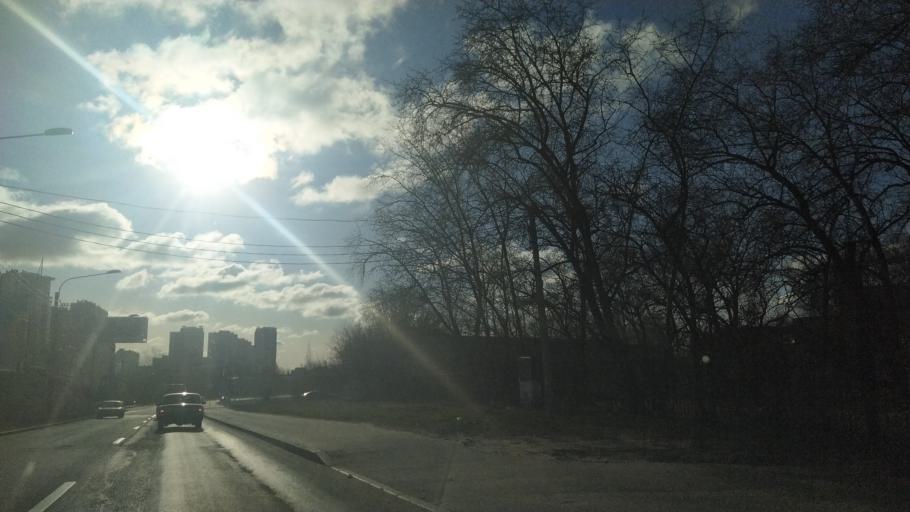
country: RU
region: Leningrad
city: Kalininskiy
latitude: 59.9937
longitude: 30.3777
